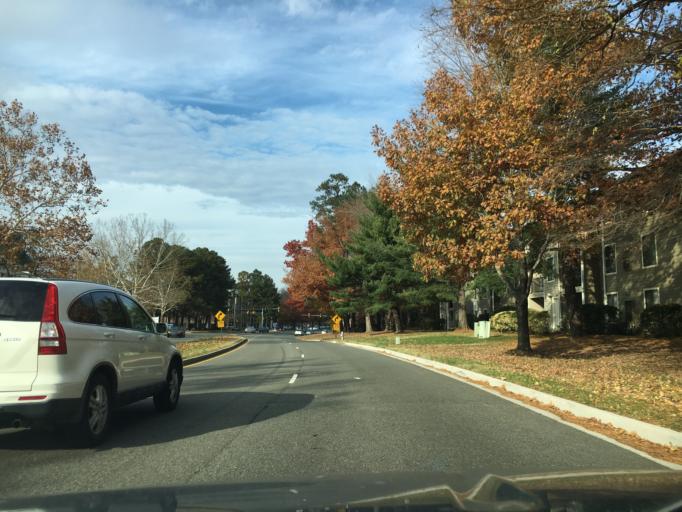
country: US
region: Virginia
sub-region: Henrico County
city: Tuckahoe
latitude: 37.6018
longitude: -77.5442
